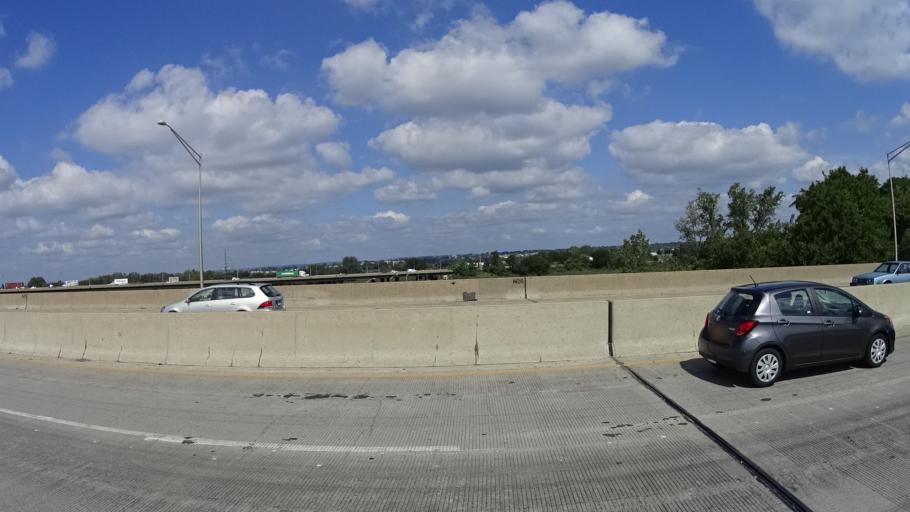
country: US
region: New Jersey
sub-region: Hudson County
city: Kearny
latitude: 40.7504
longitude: -74.1158
